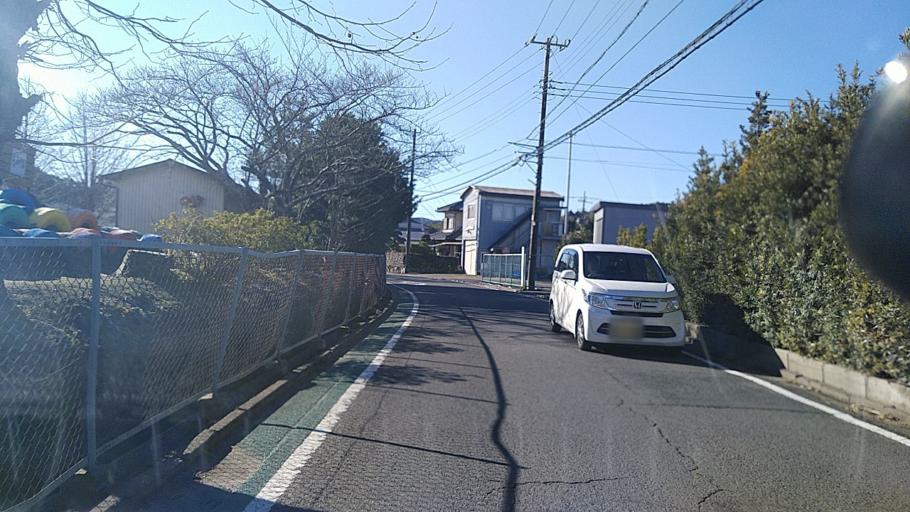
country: JP
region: Chiba
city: Kimitsu
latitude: 35.3042
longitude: 139.9579
